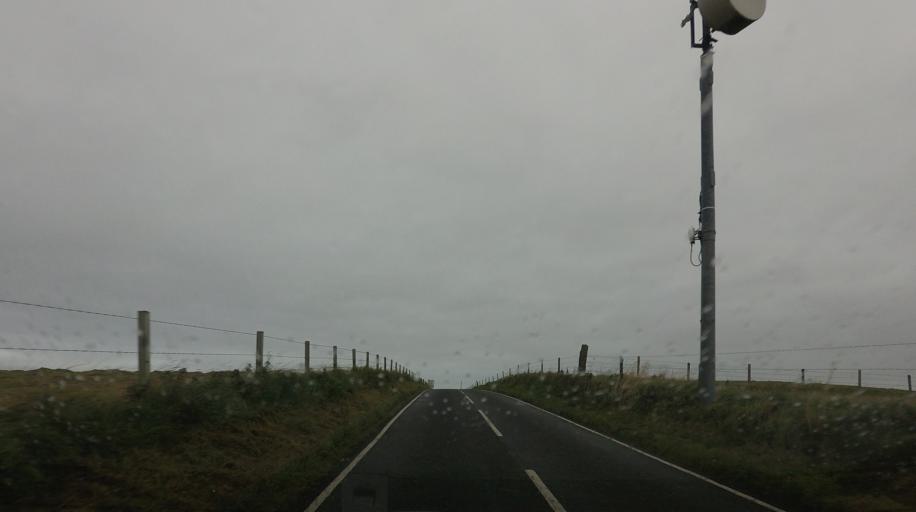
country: GB
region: Scotland
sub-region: Orkney Islands
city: Stromness
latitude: 59.1295
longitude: -3.3029
